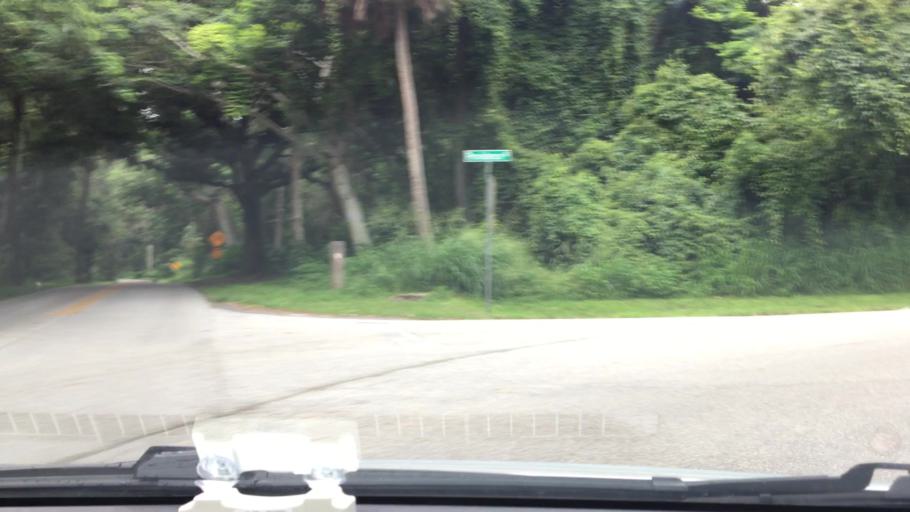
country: US
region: Florida
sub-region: Volusia County
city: Deltona
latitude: 28.8647
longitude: -81.2557
